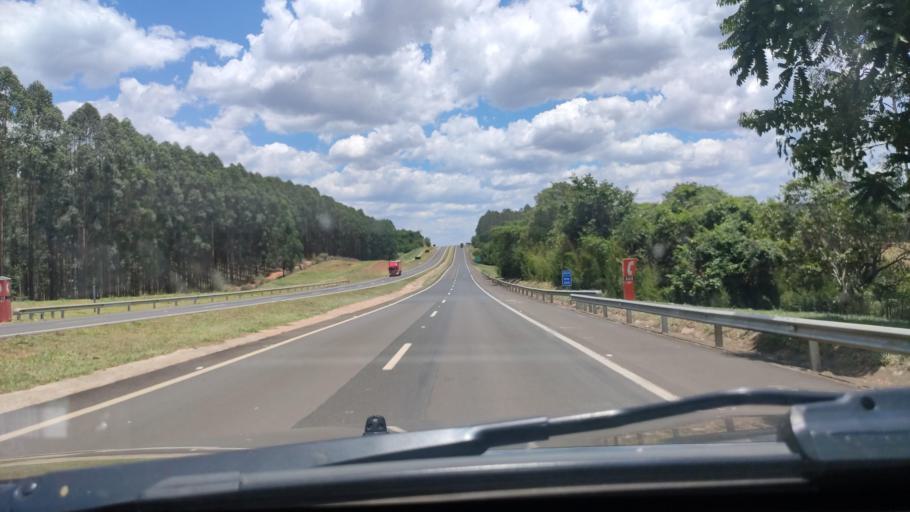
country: BR
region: Sao Paulo
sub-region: Duartina
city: Duartina
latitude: -22.4920
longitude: -49.2538
